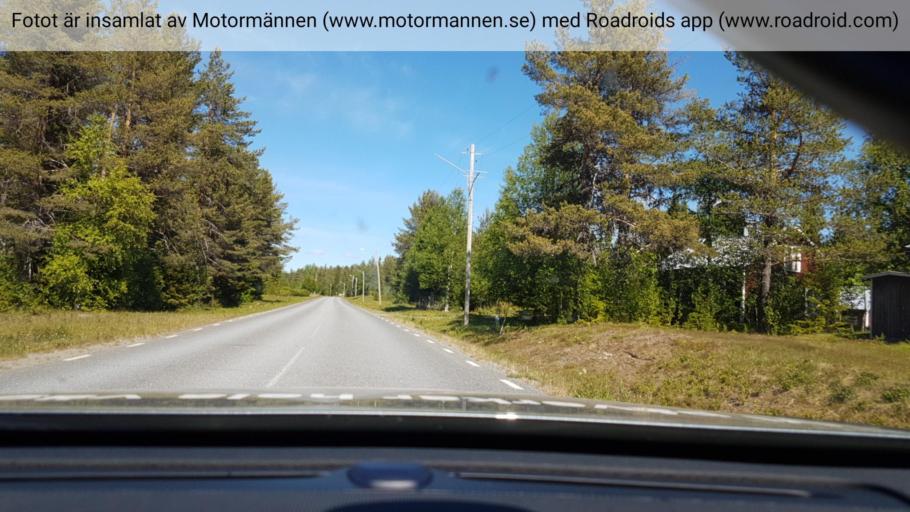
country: SE
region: Vaesterbotten
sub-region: Storumans Kommun
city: Storuman
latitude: 64.6584
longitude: 17.0963
